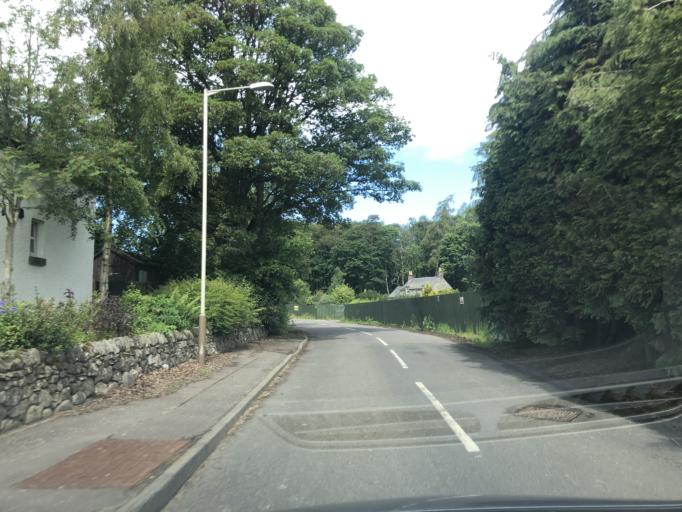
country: GB
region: Scotland
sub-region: Angus
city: Kirriemuir
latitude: 56.7288
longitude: -3.0034
